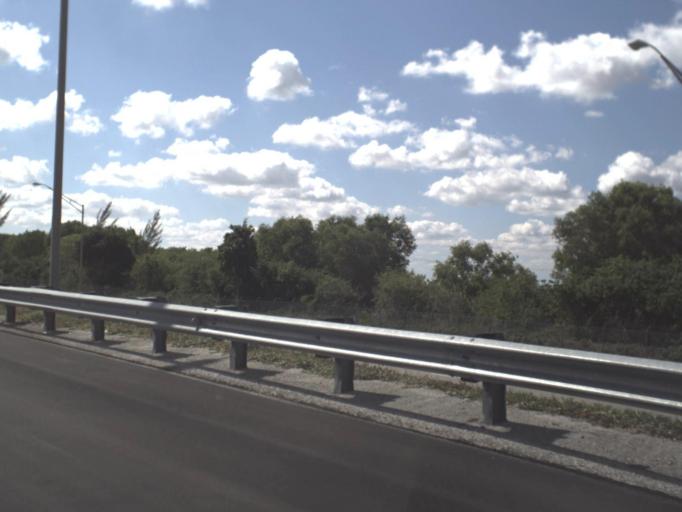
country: US
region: Florida
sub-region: Broward County
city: Weston
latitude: 26.1500
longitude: -80.3400
